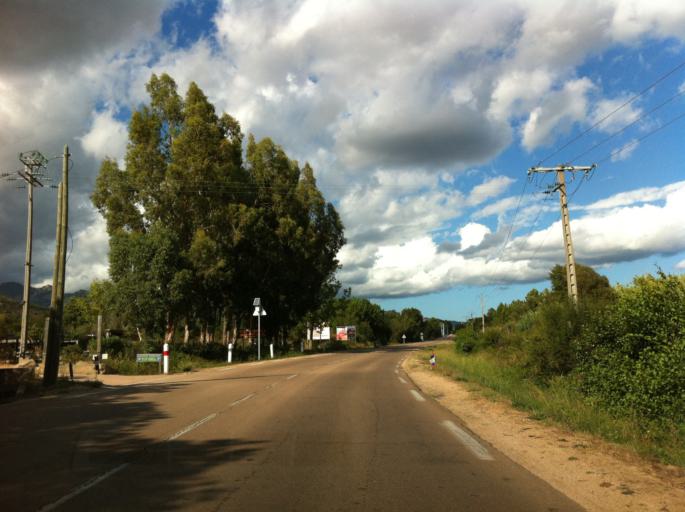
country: FR
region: Corsica
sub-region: Departement de la Corse-du-Sud
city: Porto-Vecchio
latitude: 41.6256
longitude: 9.2902
